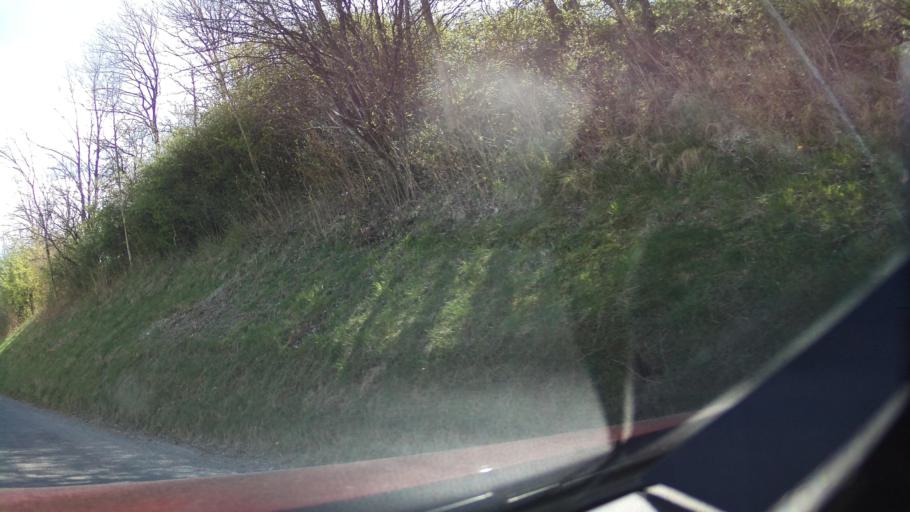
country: GB
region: England
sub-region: West Berkshire
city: Kintbury
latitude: 51.3583
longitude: -1.4732
